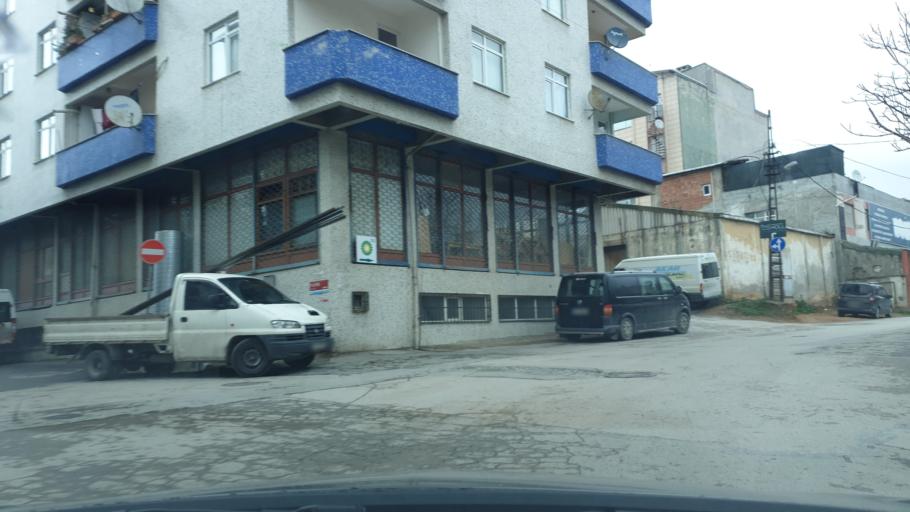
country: TR
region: Istanbul
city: Pendik
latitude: 40.8698
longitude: 29.2676
